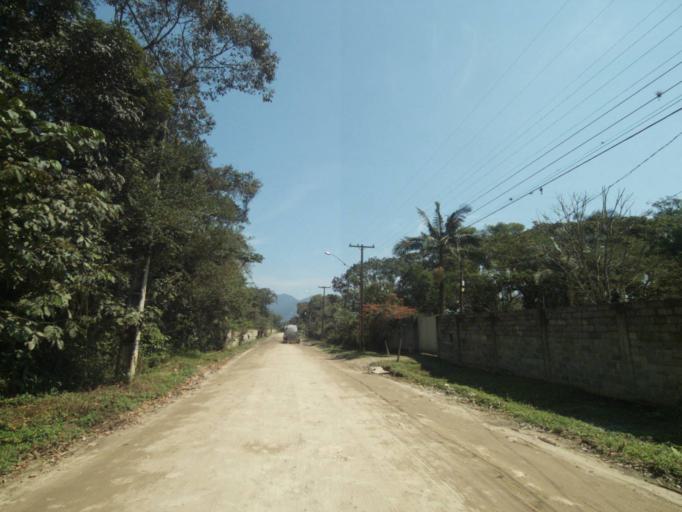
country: BR
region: Parana
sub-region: Paranagua
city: Paranagua
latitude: -25.5535
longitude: -48.5908
